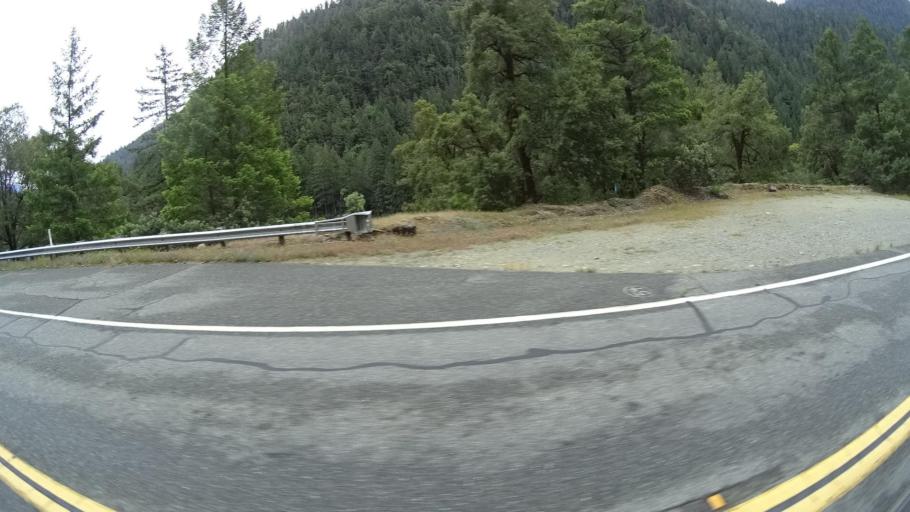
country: US
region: California
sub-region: Humboldt County
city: Willow Creek
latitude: 41.2590
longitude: -123.6191
